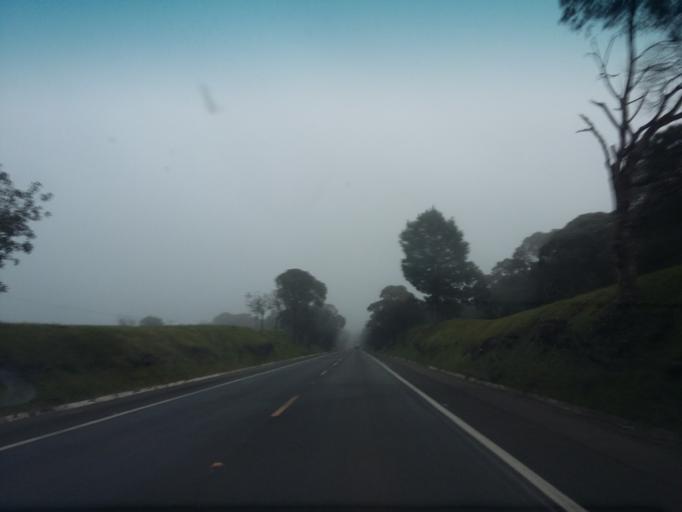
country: BR
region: Santa Catarina
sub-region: Curitibanos
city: Curitibanos
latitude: -27.2484
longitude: -50.4570
